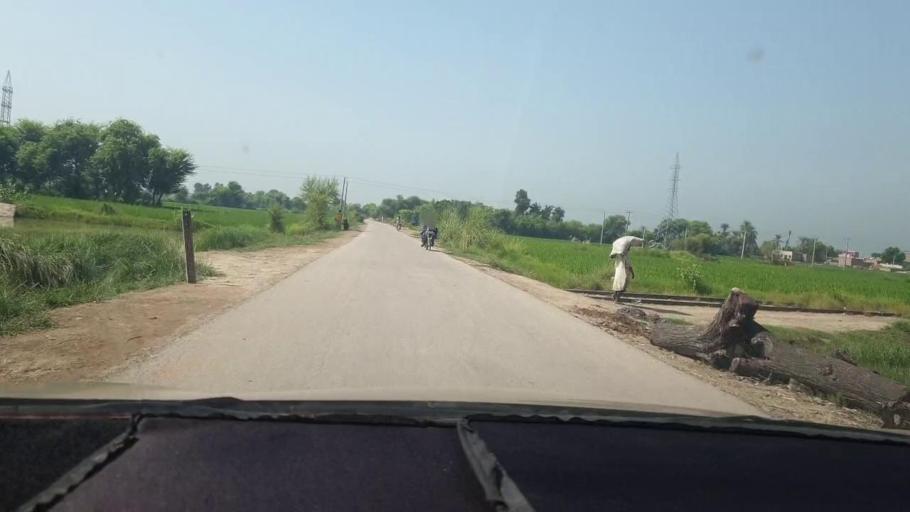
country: PK
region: Sindh
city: Kambar
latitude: 27.5867
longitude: 68.0489
